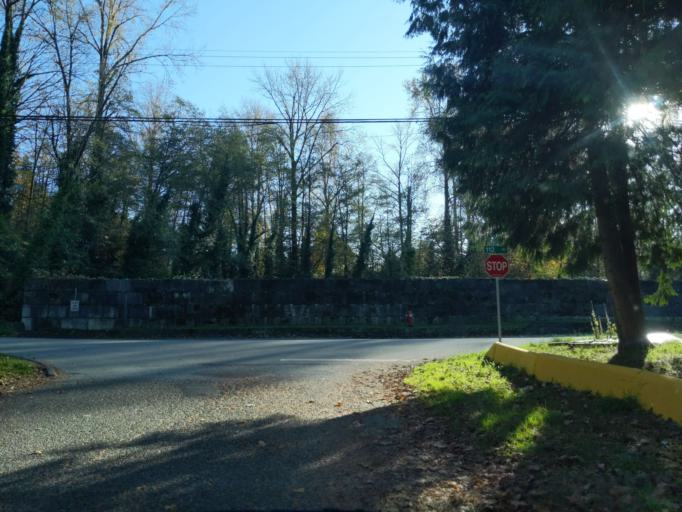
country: CA
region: British Columbia
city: New Westminster
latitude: 49.2065
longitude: -122.8592
